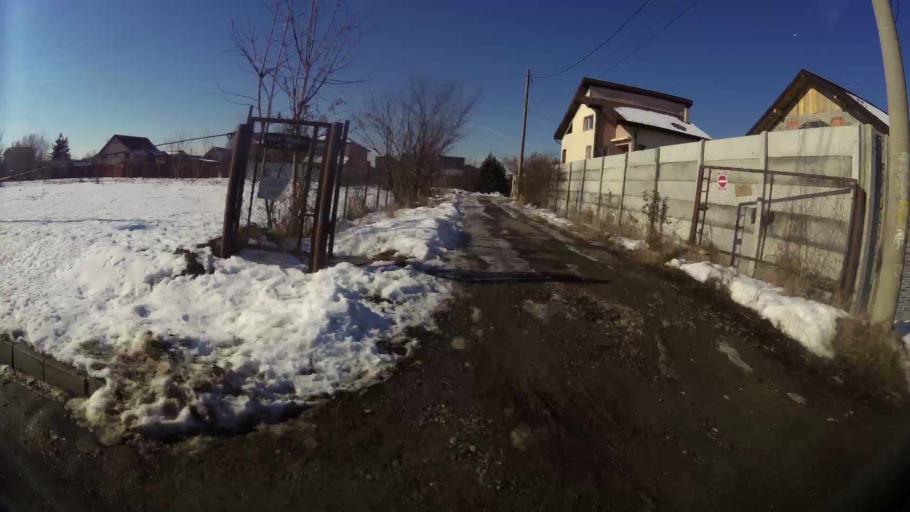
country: RO
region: Ilfov
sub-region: Comuna Magurele
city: Magurele
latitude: 44.3843
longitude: 26.0521
